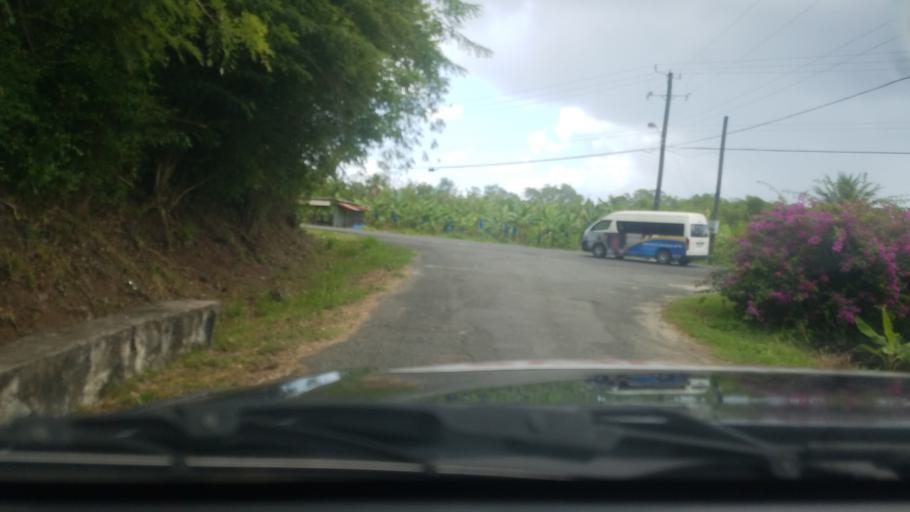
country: LC
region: Praslin
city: Praslin
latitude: 13.8711
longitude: -60.8993
